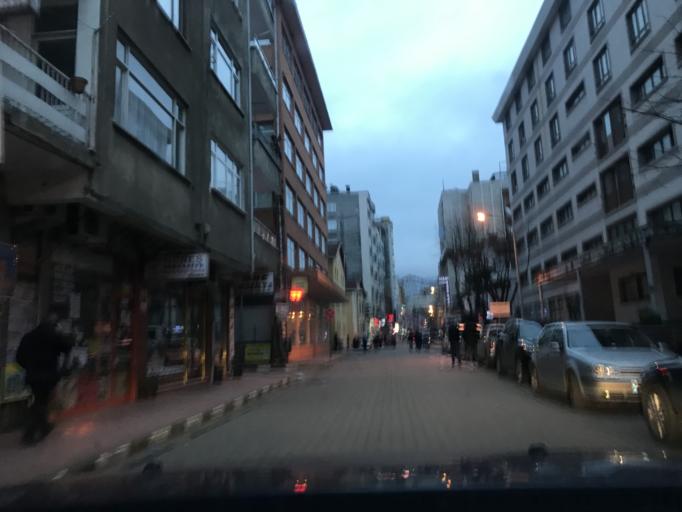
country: TR
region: Trabzon
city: Akcaabat
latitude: 41.0211
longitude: 39.5735
